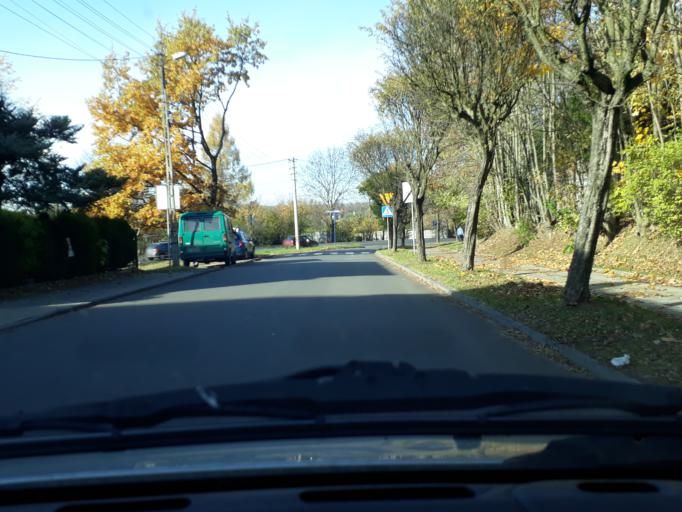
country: PL
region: Silesian Voivodeship
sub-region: Powiat tarnogorski
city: Tarnowskie Gory
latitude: 50.4367
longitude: 18.8635
